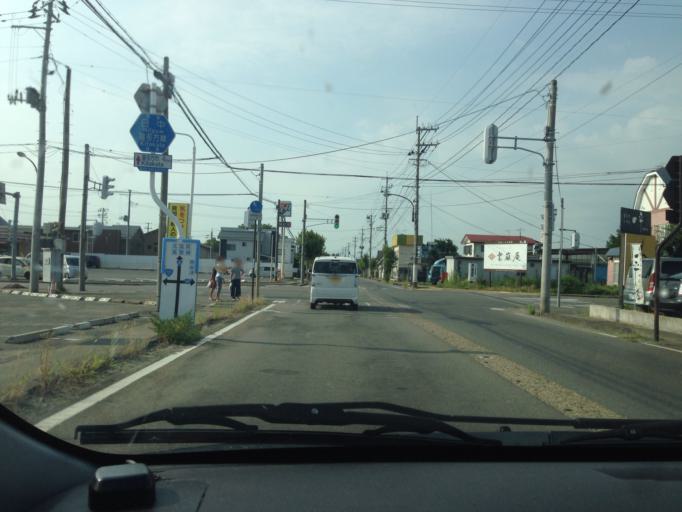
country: JP
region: Fukushima
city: Kitakata
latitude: 37.6660
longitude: 139.8717
